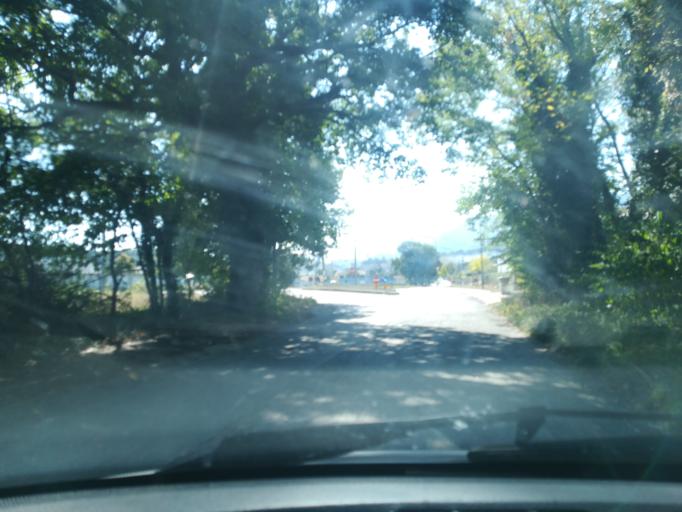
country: IT
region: The Marches
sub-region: Provincia di Macerata
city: Caldarola
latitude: 43.1487
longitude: 13.2242
